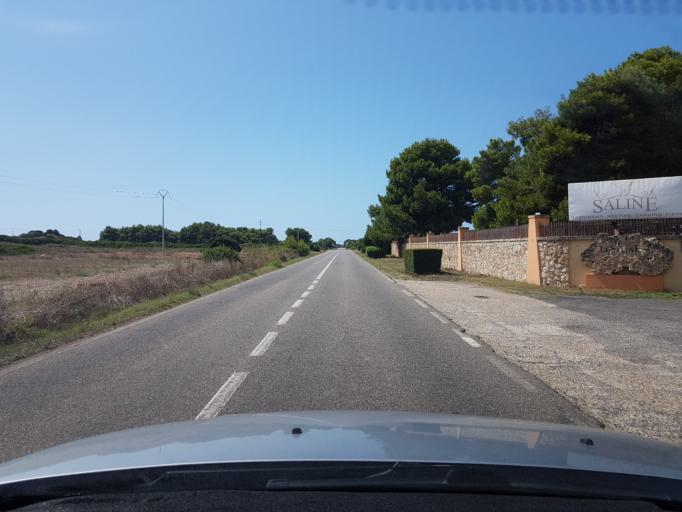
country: IT
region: Sardinia
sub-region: Provincia di Oristano
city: Riola Sardo
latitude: 40.0219
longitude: 8.4521
